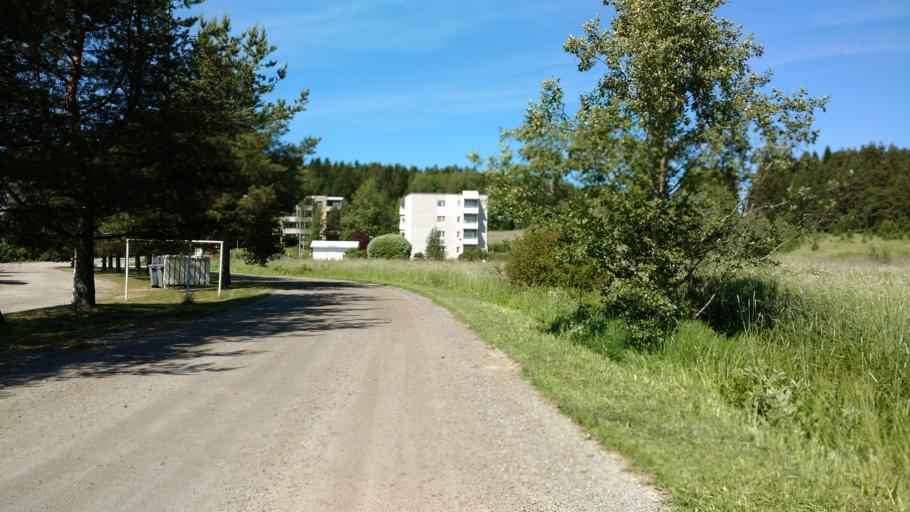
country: FI
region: Varsinais-Suomi
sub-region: Salo
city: Salo
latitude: 60.4039
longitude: 23.1475
